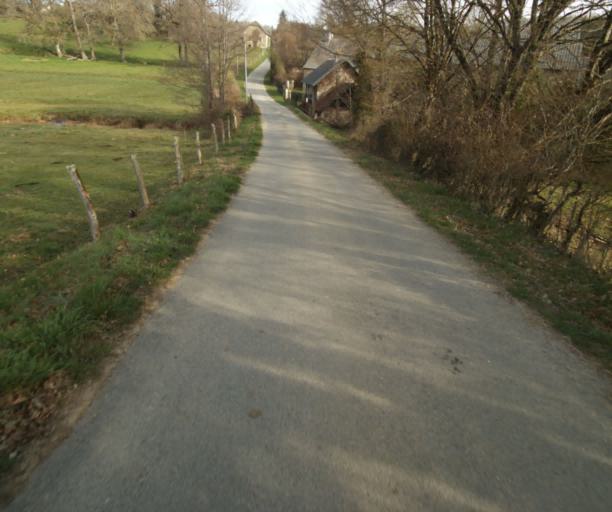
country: FR
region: Limousin
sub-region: Departement de la Correze
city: Chamboulive
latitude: 45.4438
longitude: 1.7539
